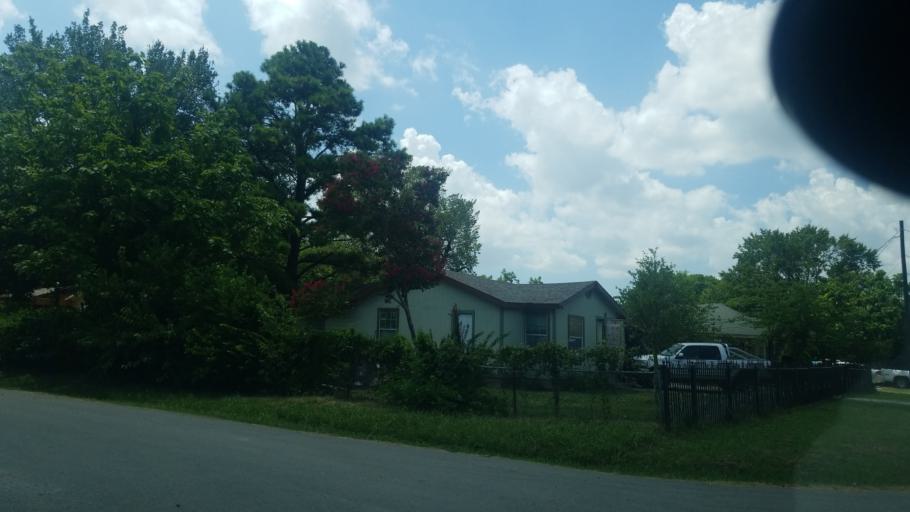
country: US
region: Texas
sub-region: Dallas County
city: Dallas
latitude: 32.7168
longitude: -96.7629
